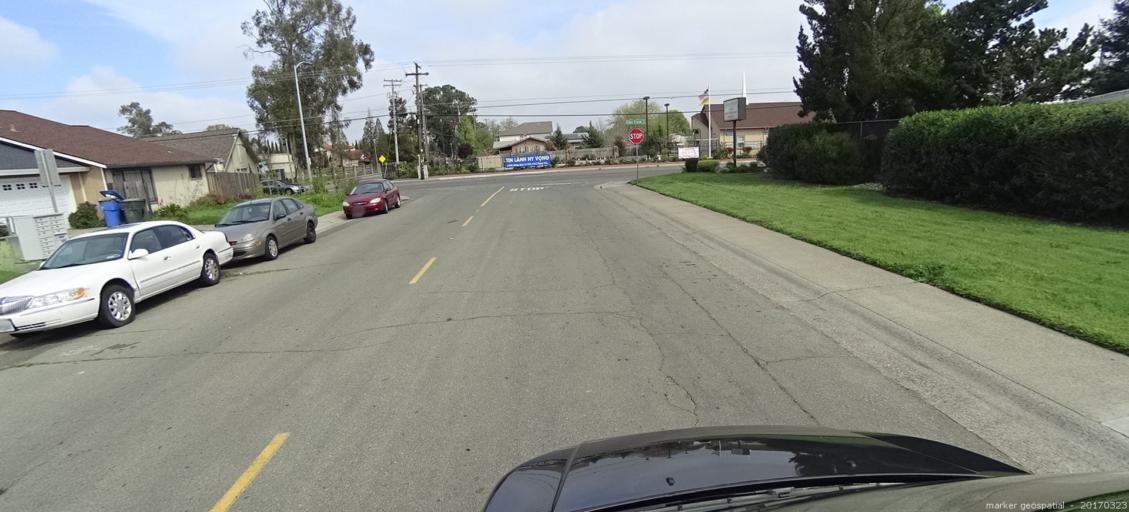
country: US
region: California
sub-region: Sacramento County
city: Florin
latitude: 38.5101
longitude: -121.4296
